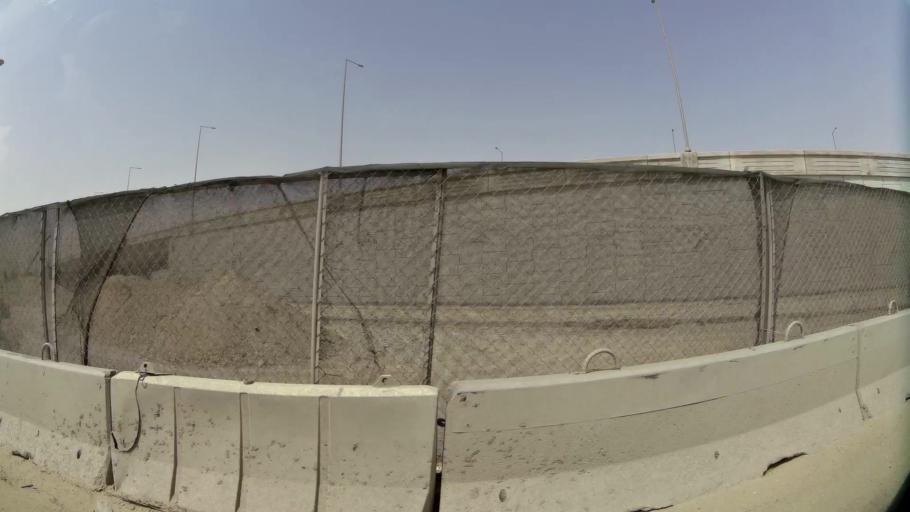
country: QA
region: Al Wakrah
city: Al Wukayr
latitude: 25.1928
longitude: 51.4568
